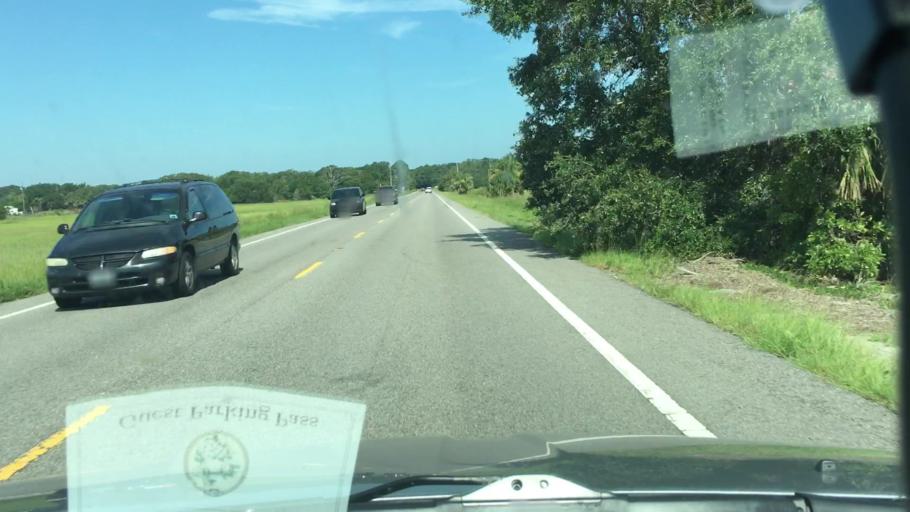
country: US
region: South Carolina
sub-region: Beaufort County
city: Beaufort
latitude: 32.4117
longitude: -80.4741
